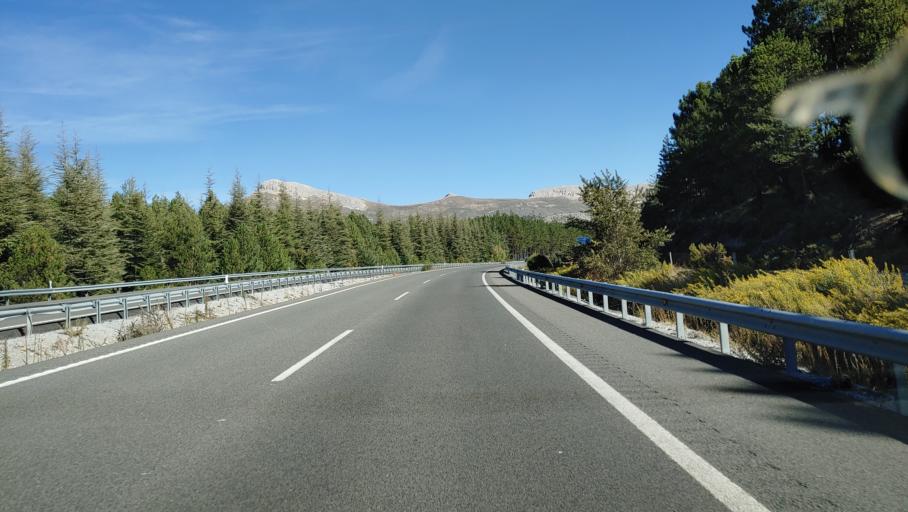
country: ES
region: Andalusia
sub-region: Provincia de Granada
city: Beas de Granada
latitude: 37.2834
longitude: -3.4575
